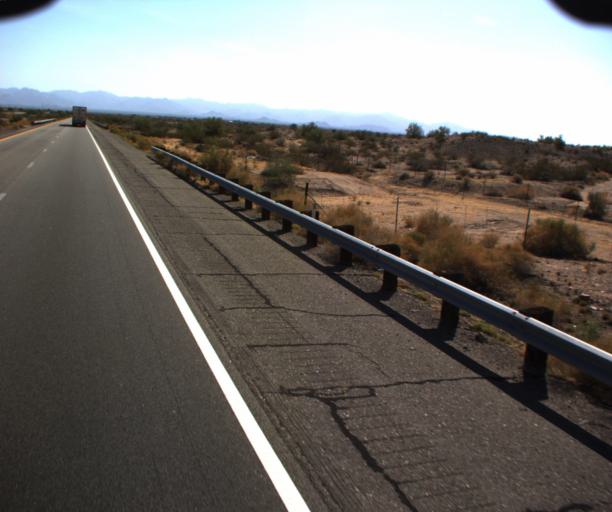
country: US
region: Arizona
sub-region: Mohave County
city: Desert Hills
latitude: 34.7427
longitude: -114.2383
